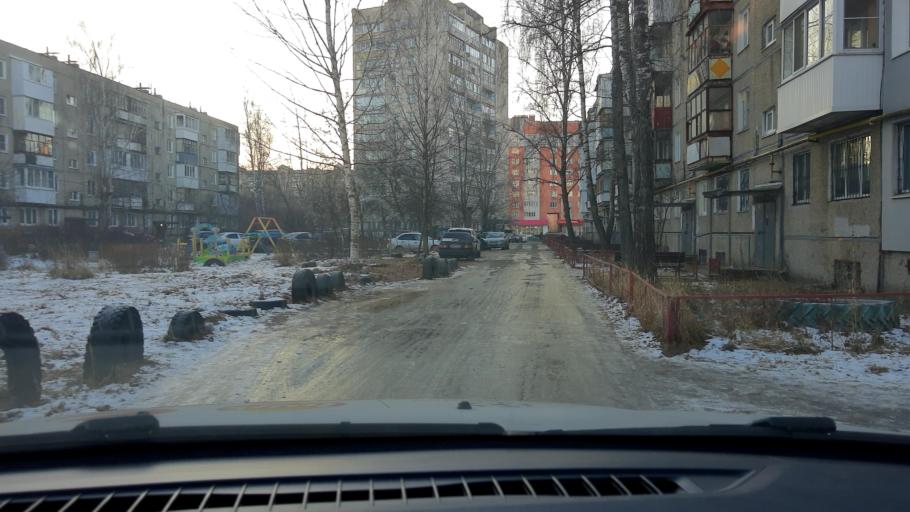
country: RU
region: Nizjnij Novgorod
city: Dzerzhinsk
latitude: 56.2320
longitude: 43.4030
